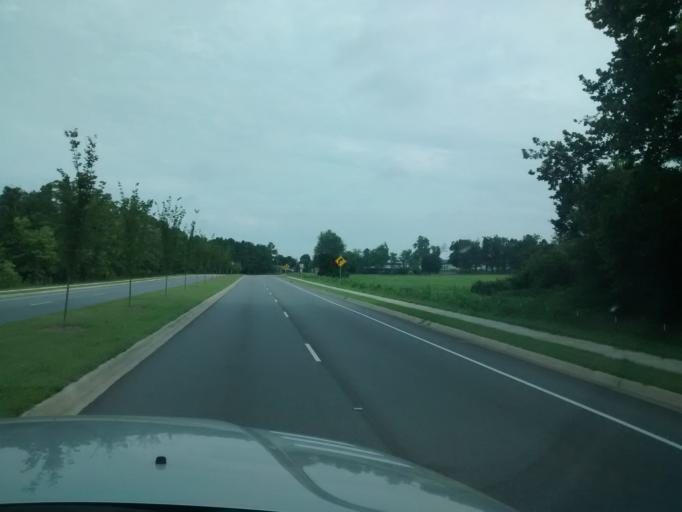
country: US
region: Arkansas
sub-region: Washington County
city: Springdale
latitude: 36.1455
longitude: -94.1179
